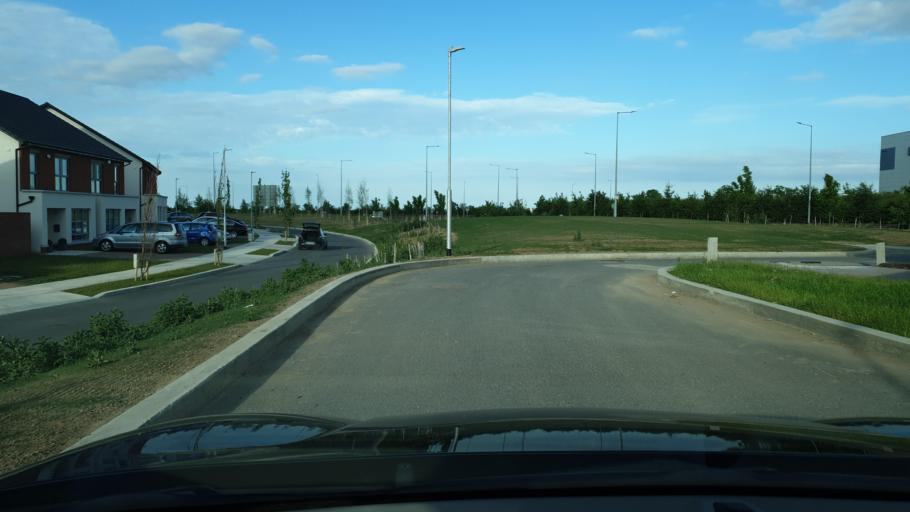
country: IE
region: Leinster
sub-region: Fingal County
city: Blanchardstown
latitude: 53.4231
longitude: -6.3657
